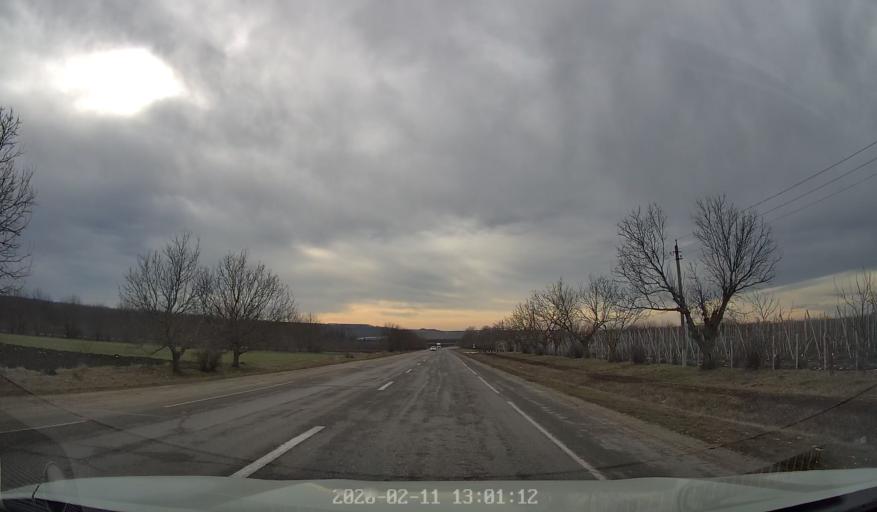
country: MD
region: Briceni
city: Briceni
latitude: 48.3206
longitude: 27.0060
